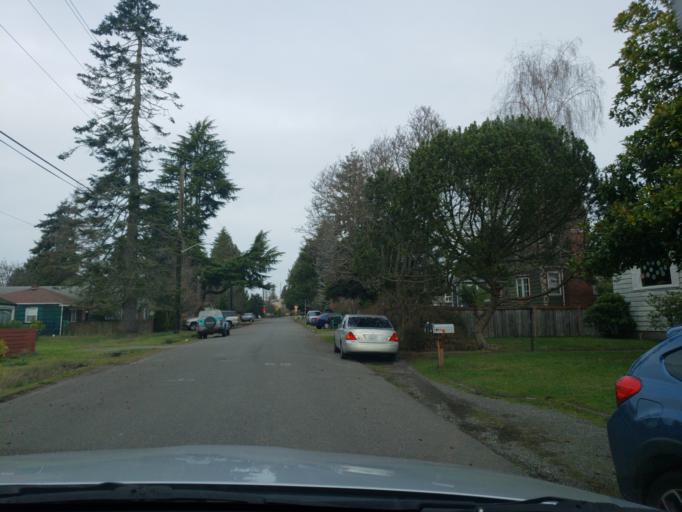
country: US
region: Washington
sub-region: King County
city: Shoreline
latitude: 47.7003
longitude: -122.3512
